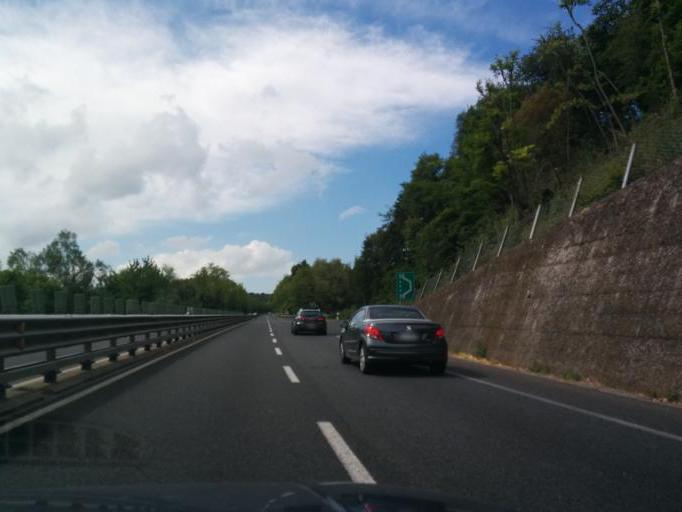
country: IT
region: Tuscany
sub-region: Province of Florence
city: Sambuca
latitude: 43.5642
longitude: 11.2133
